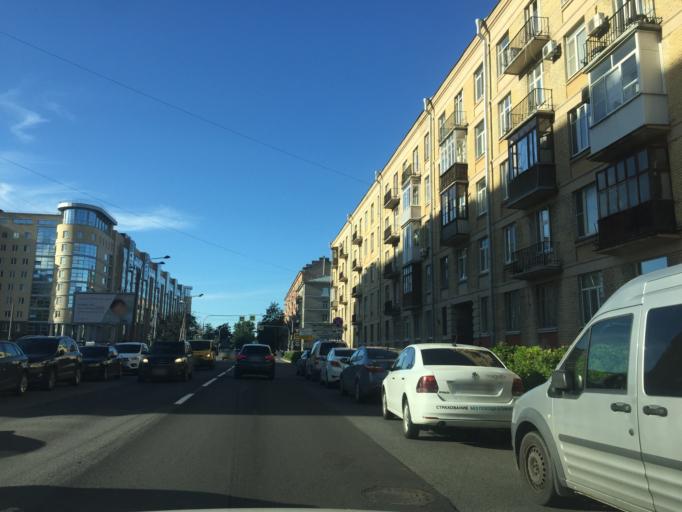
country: RU
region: St.-Petersburg
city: Admiralteisky
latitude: 59.8746
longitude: 30.3136
